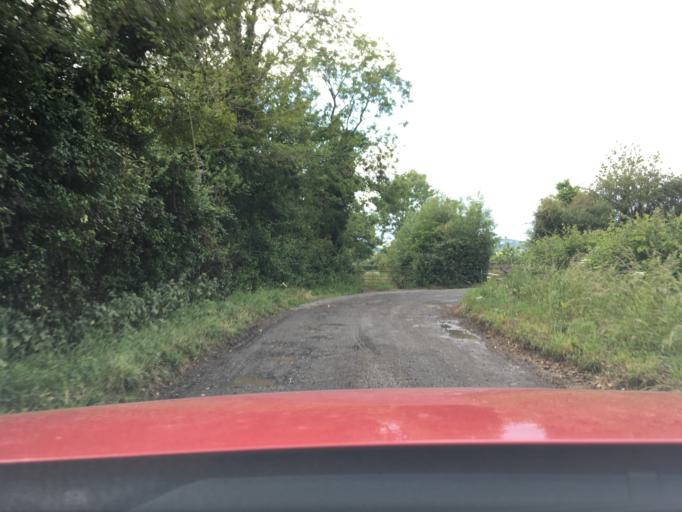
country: GB
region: England
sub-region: Gloucestershire
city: Cinderford
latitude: 51.8024
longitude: -2.4210
